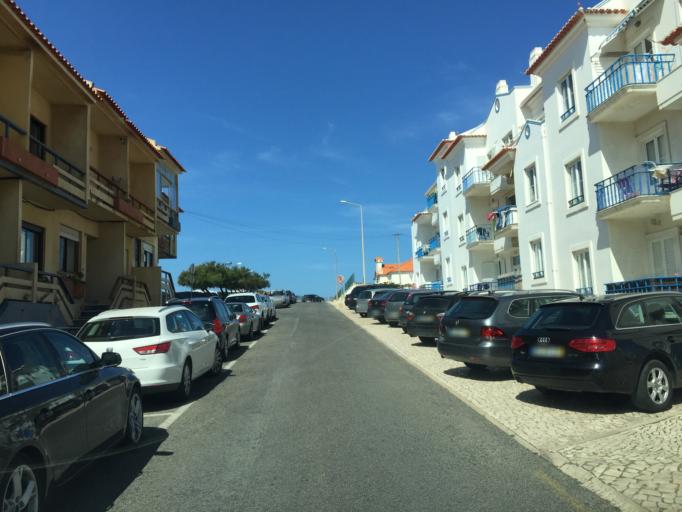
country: PT
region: Lisbon
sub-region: Torres Vedras
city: Silveira
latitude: 39.1327
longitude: -9.3829
